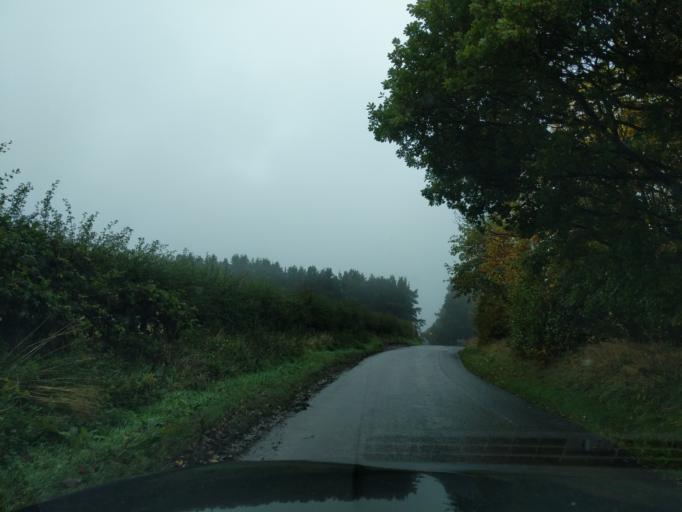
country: GB
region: Scotland
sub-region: East Lothian
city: Dunbar
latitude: 55.9327
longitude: -2.4125
